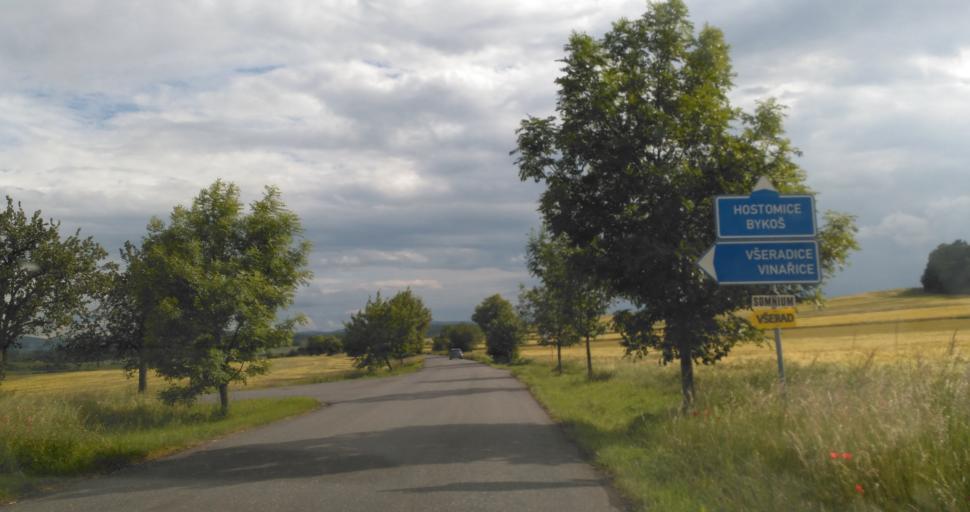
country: CZ
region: Central Bohemia
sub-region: Okres Beroun
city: Kraluv Dvur
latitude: 49.8955
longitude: 14.0755
